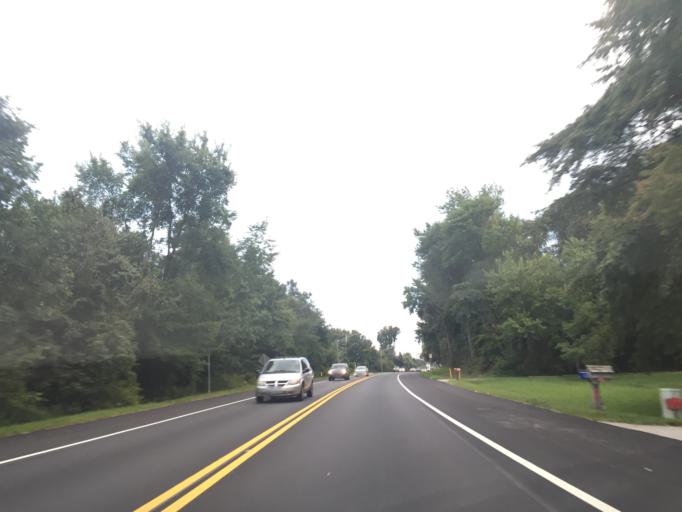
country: US
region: Maryland
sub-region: Anne Arundel County
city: Severn
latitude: 39.1426
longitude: -76.6851
